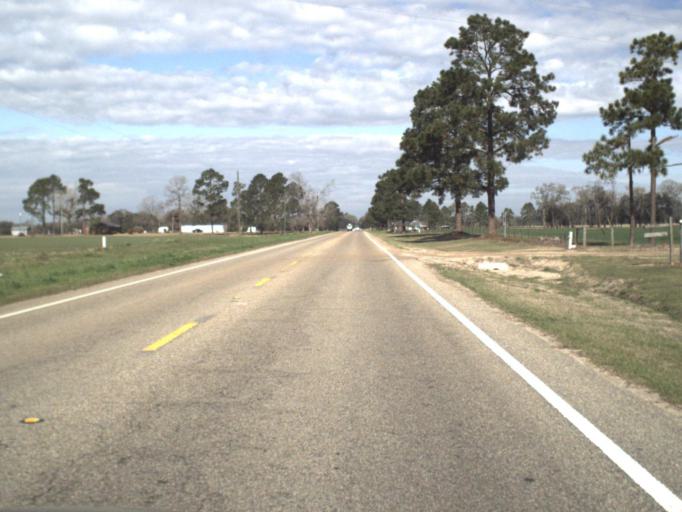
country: US
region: Florida
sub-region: Jackson County
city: Malone
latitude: 30.9747
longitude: -85.1685
